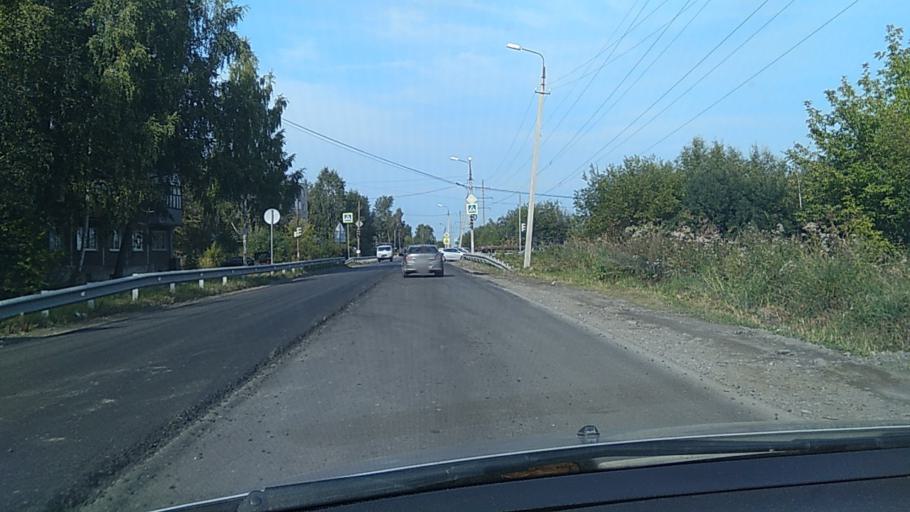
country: RU
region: Sverdlovsk
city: Sredneuralsk
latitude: 56.9815
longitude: 60.4760
